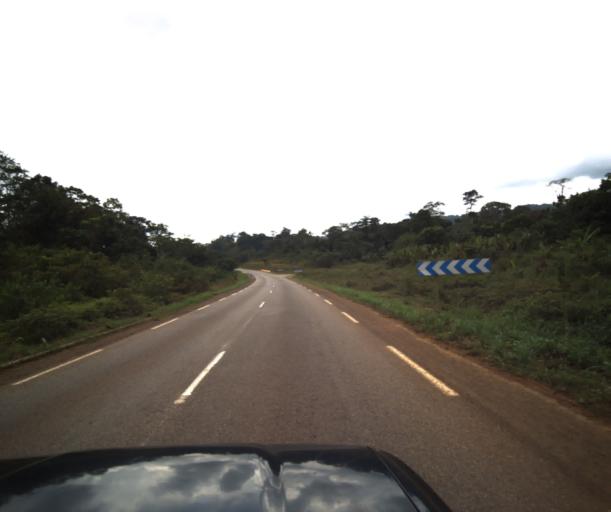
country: CM
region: Littoral
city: Edea
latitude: 3.8327
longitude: 10.4045
